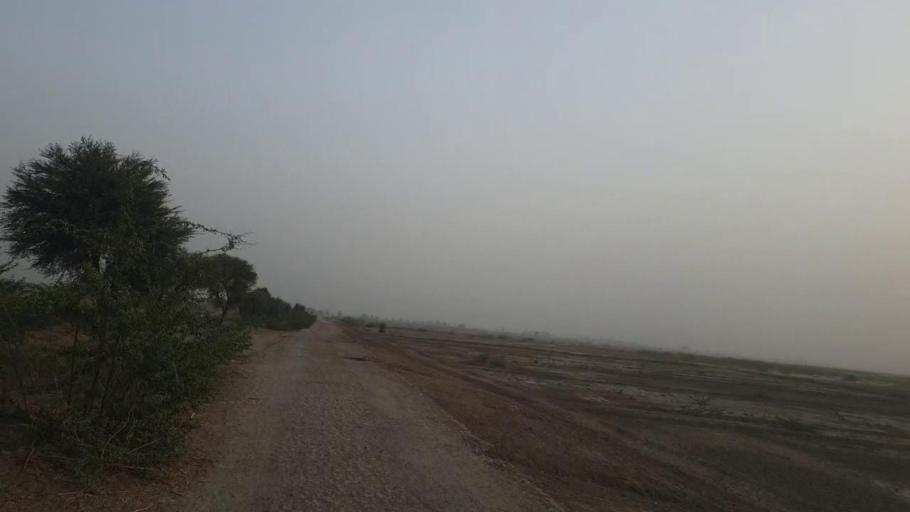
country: PK
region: Sindh
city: Kunri
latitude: 25.1133
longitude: 69.5527
